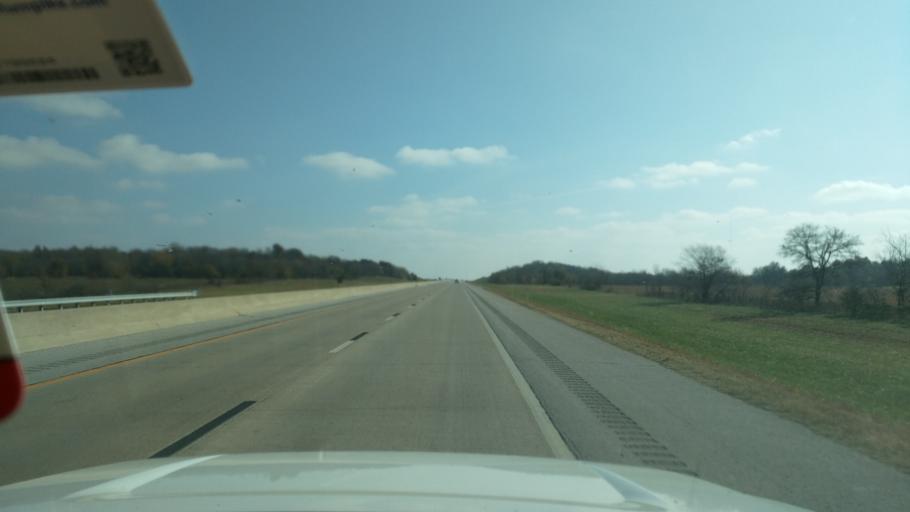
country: US
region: Oklahoma
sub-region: Wagoner County
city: Coweta
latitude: 36.0062
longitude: -95.6534
